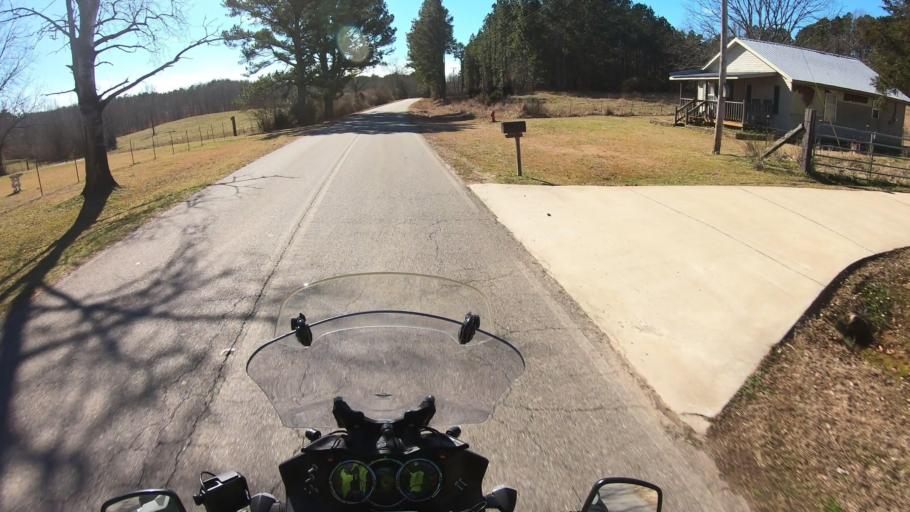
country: US
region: Alabama
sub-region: Clay County
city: Lineville
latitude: 33.3901
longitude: -85.8126
